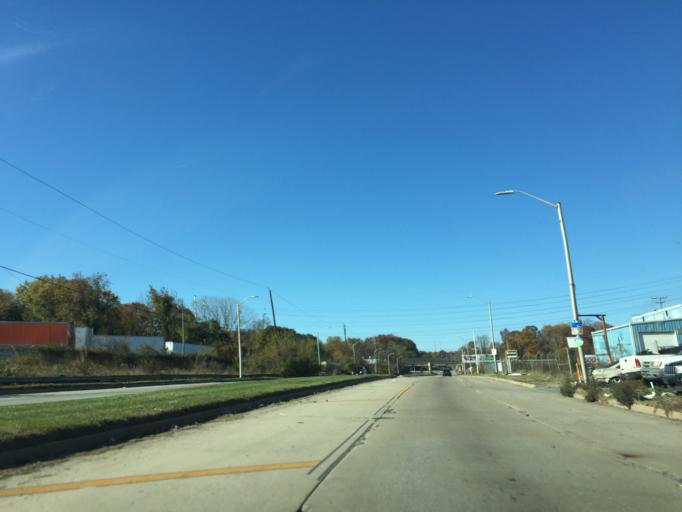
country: US
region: Maryland
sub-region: Baltimore County
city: Baltimore Highlands
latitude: 39.2416
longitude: -76.6265
